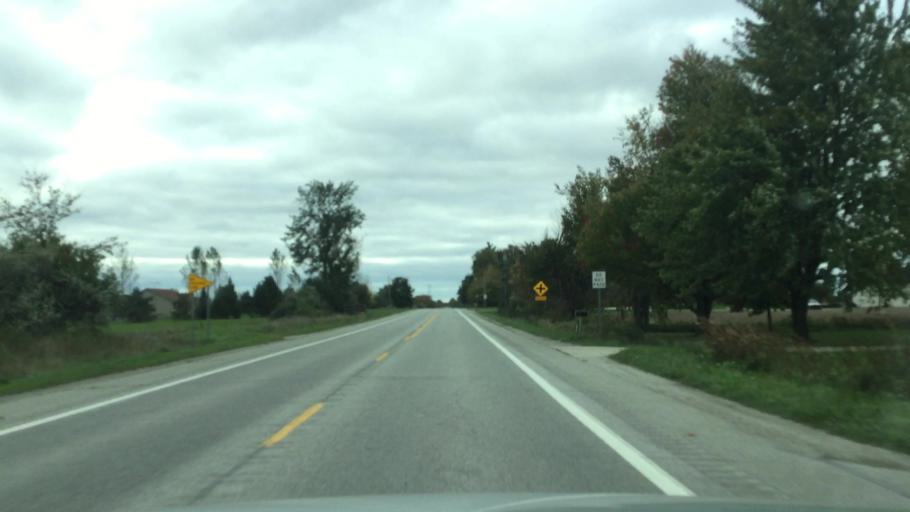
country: US
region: Michigan
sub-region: Macomb County
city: Memphis
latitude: 42.9431
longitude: -82.7623
